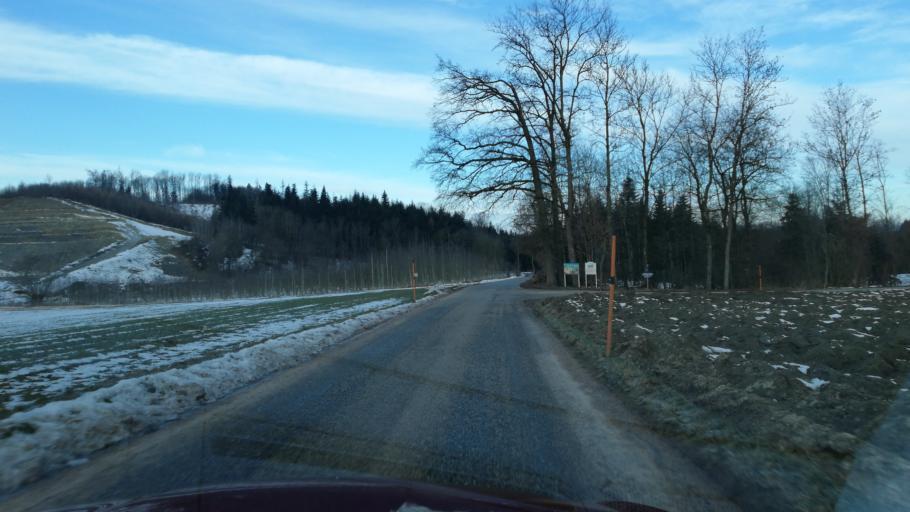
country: AT
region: Upper Austria
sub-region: Wels-Land
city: Buchkirchen
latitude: 48.2342
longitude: 13.9955
